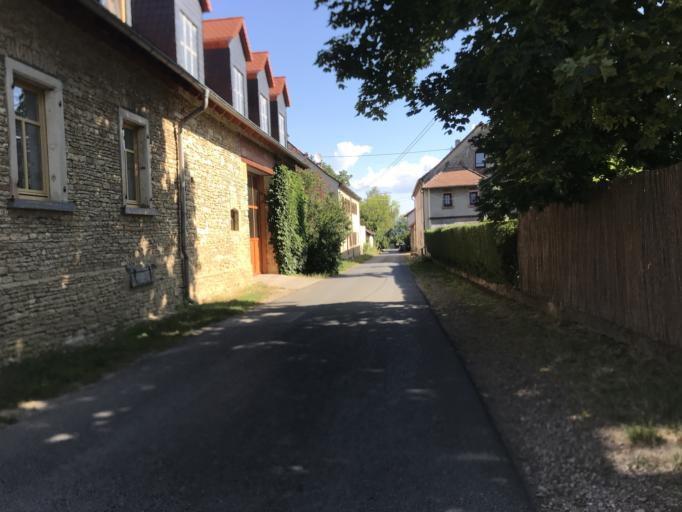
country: DE
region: Rheinland-Pfalz
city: Ockenheim
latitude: 49.9303
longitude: 7.9988
